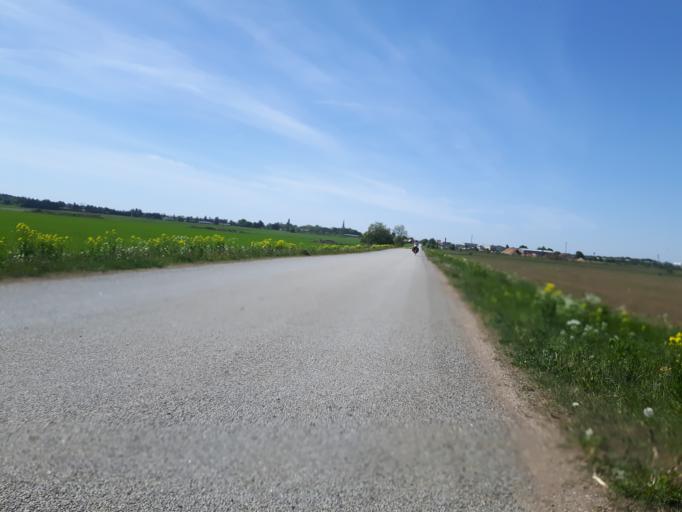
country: EE
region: Ida-Virumaa
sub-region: Aseri vald
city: Aseri
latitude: 59.4554
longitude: 26.7060
